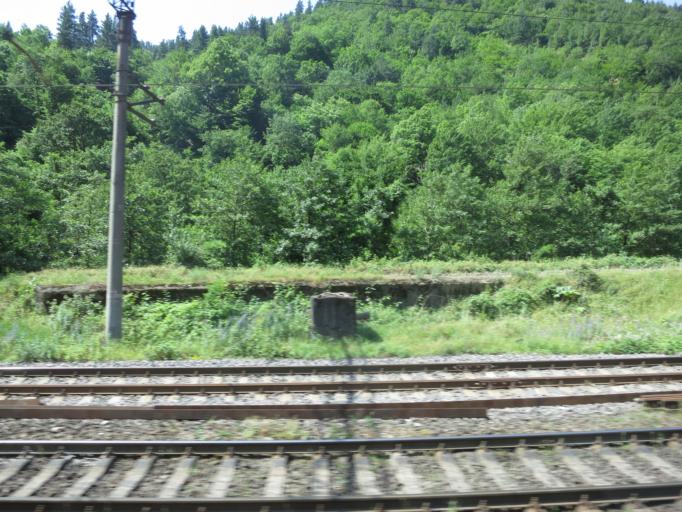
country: GE
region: Imereti
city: Kharagauli
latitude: 41.9746
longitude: 43.3010
